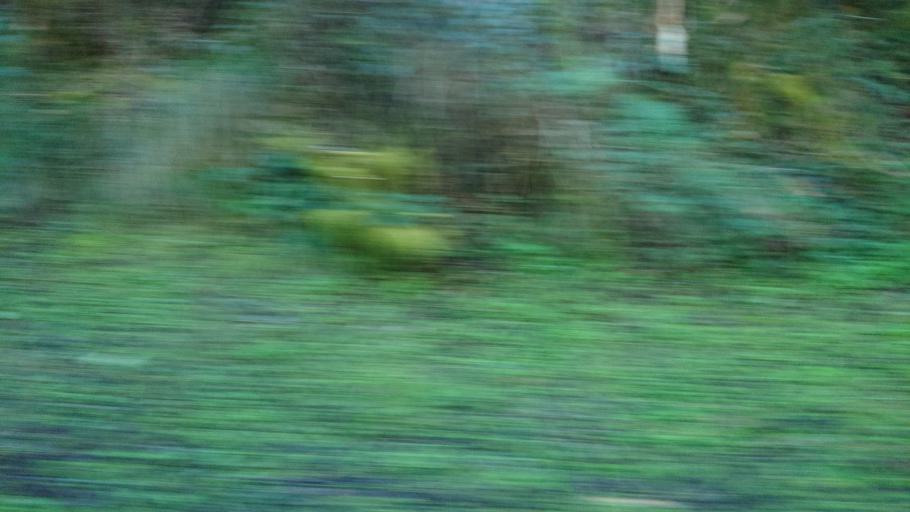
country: TW
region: Taiwan
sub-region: Hualien
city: Hualian
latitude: 24.3798
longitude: 121.3424
